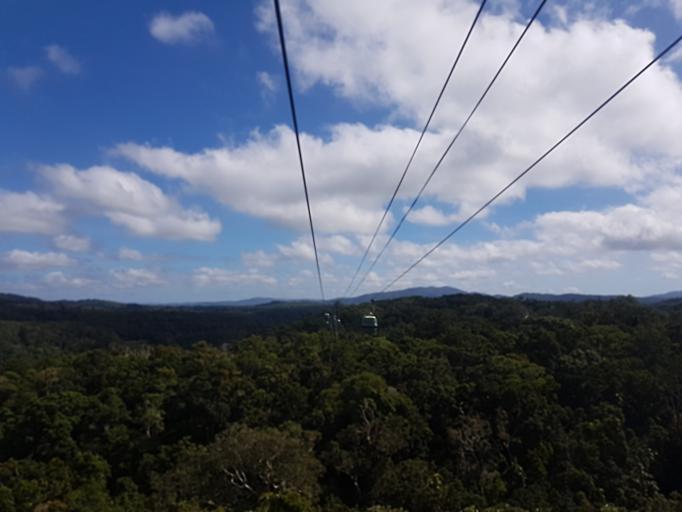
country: AU
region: Queensland
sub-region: Tablelands
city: Kuranda
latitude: -16.8388
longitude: 145.6536
